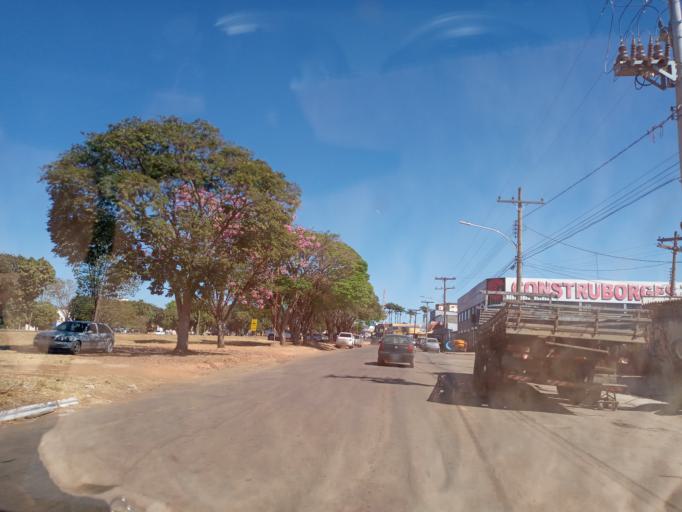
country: BR
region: Goias
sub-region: Abadiania
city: Abadiania
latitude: -16.0910
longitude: -48.4952
